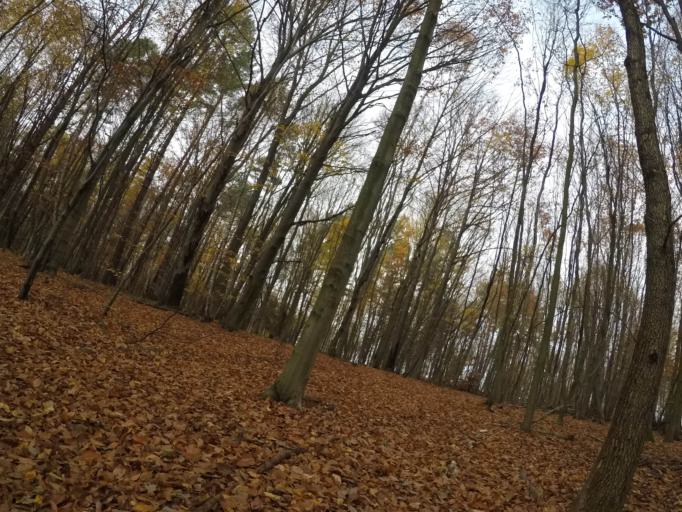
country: SK
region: Presovsky
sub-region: Okres Presov
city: Presov
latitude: 48.9521
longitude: 21.2041
